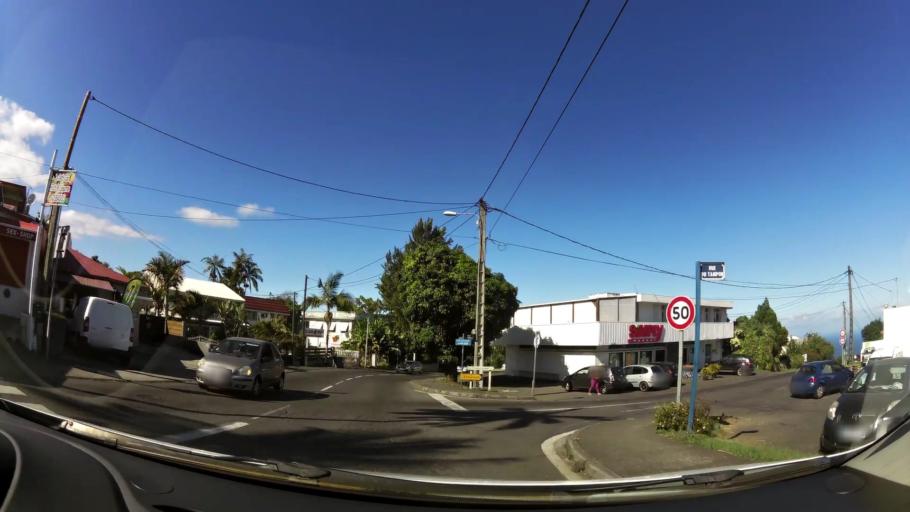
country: RE
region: Reunion
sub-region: Reunion
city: Le Tampon
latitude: -21.2792
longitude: 55.5251
